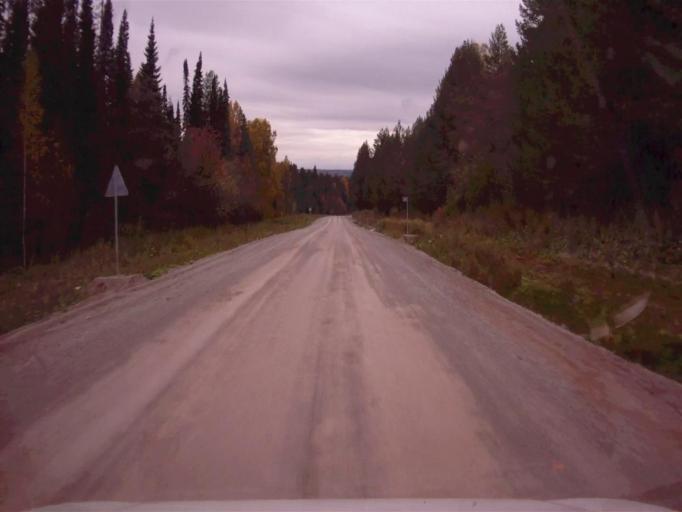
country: RU
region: Chelyabinsk
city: Nyazepetrovsk
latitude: 56.0510
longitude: 59.5321
